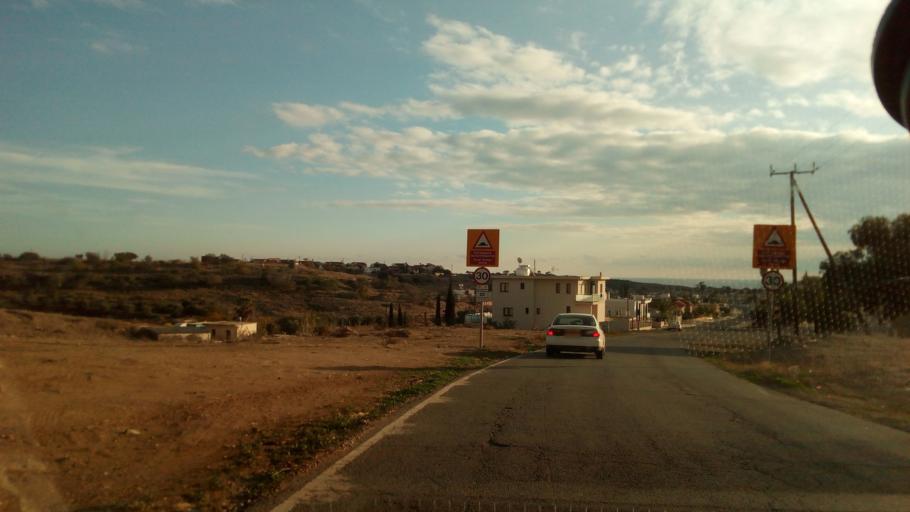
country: CY
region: Larnaka
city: Xylotymbou
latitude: 34.9978
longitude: 33.7837
